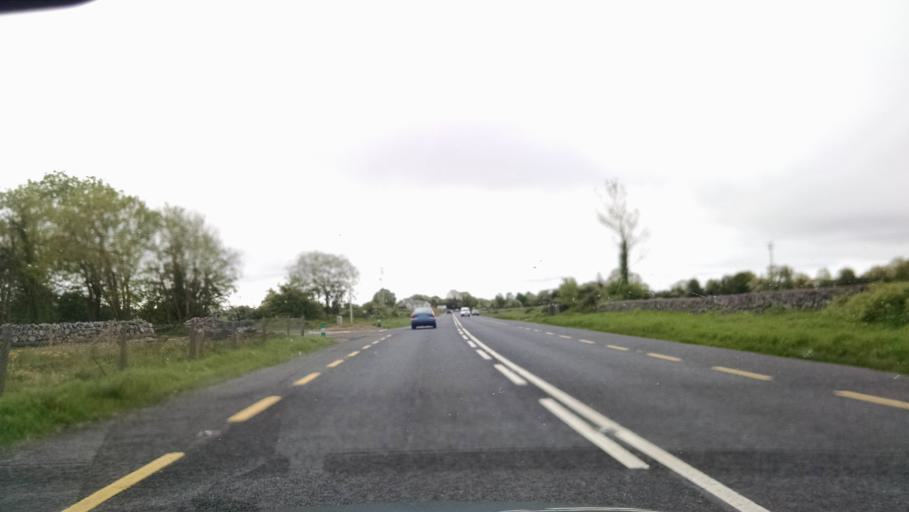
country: IE
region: Connaught
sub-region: County Galway
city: Claregalway
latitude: 53.4073
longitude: -9.0173
